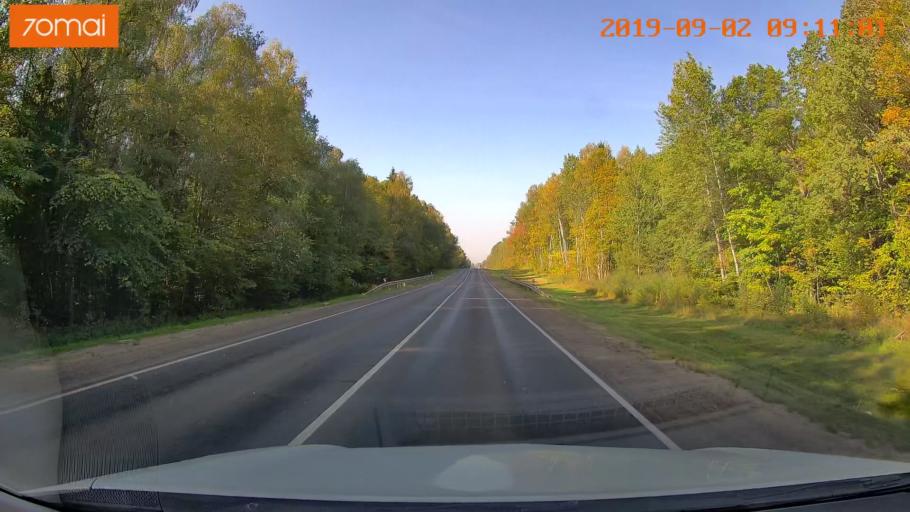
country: RU
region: Kaluga
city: Myatlevo
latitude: 54.8711
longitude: 35.5860
